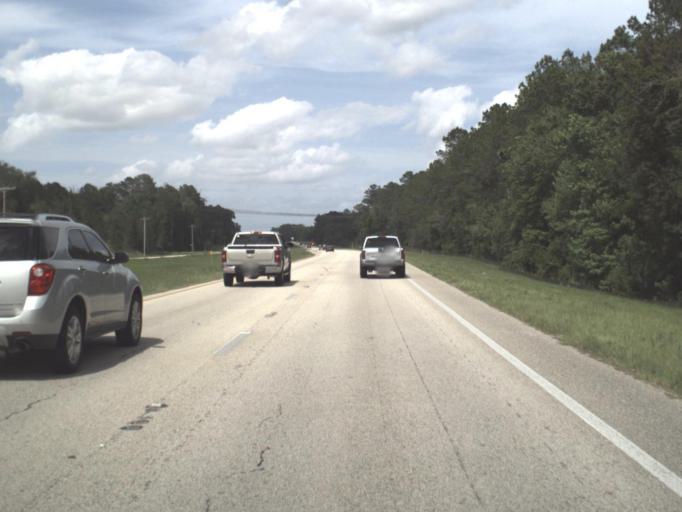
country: US
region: Florida
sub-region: Clay County
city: Middleburg
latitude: 30.0944
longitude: -81.8448
